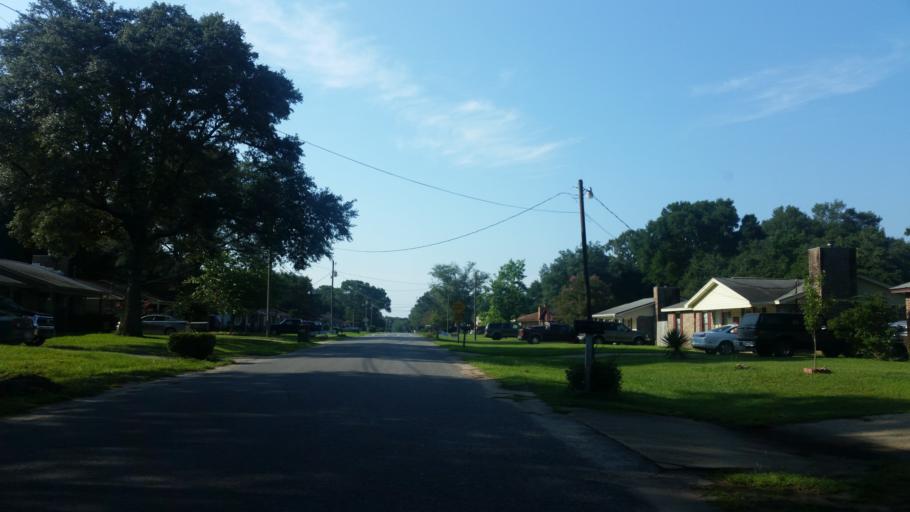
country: US
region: Florida
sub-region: Escambia County
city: Bellview
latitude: 30.4750
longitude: -87.2951
